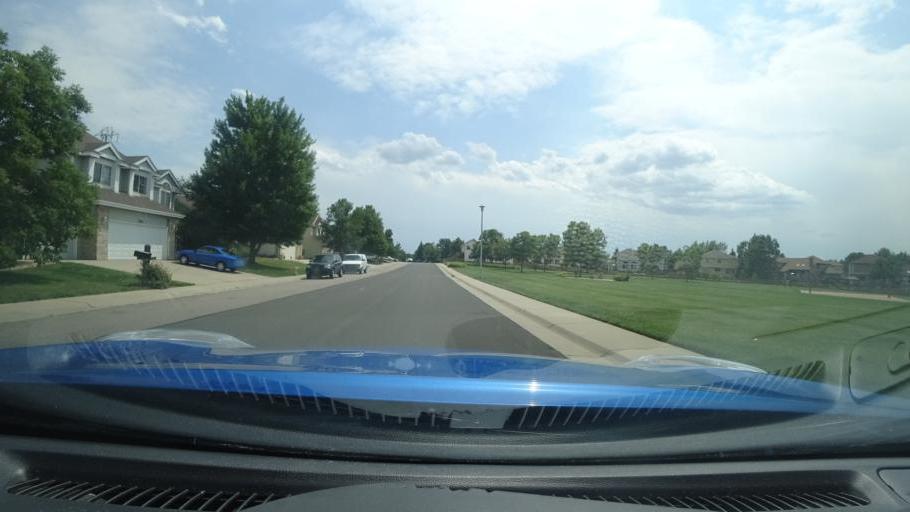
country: US
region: Colorado
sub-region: Adams County
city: Aurora
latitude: 39.6744
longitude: -104.7733
